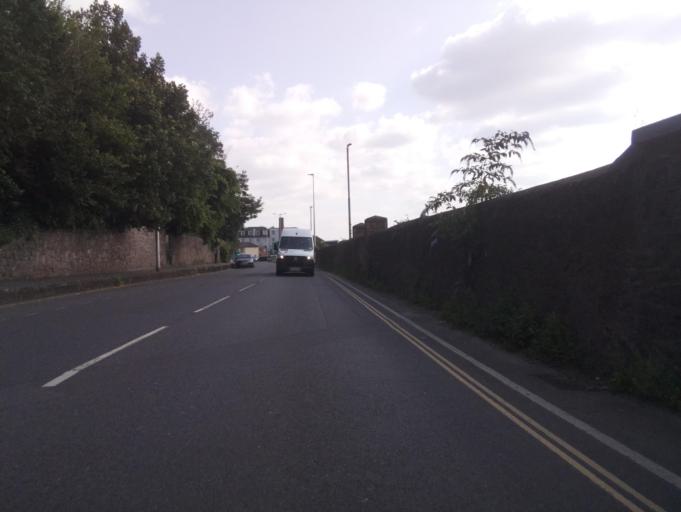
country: GB
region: England
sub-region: Devon
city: Exeter
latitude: 50.7322
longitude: -3.5433
